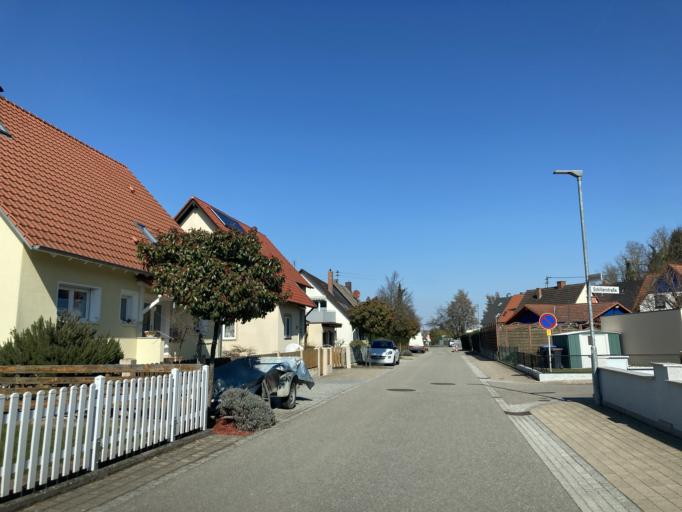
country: DE
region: Baden-Wuerttemberg
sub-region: Freiburg Region
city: Buggingen
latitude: 47.8524
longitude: 7.6386
